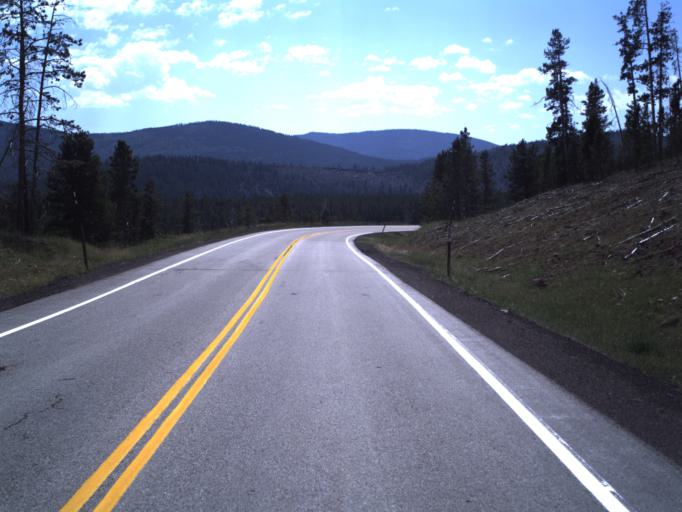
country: US
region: Utah
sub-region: Daggett County
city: Manila
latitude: 40.8357
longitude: -109.4638
